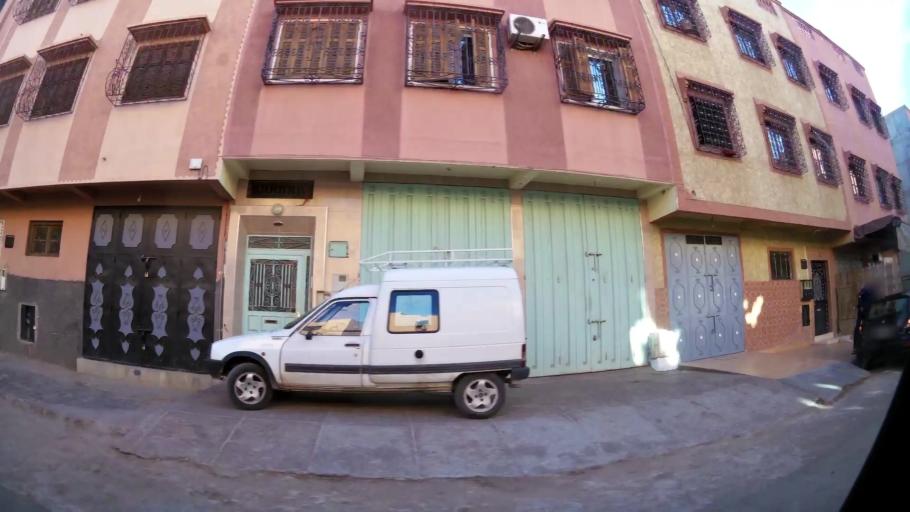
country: MA
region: Marrakech-Tensift-Al Haouz
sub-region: Marrakech
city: Marrakesh
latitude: 31.6161
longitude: -8.0689
